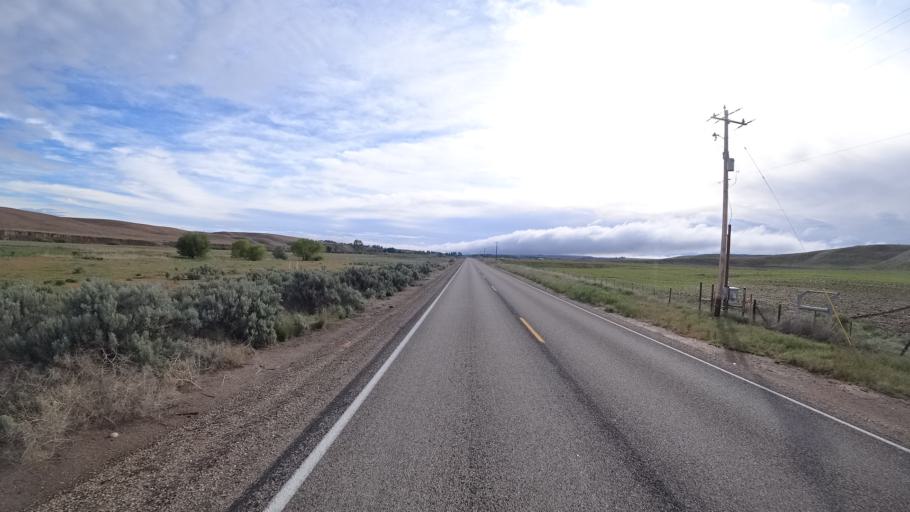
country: US
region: Idaho
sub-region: Ada County
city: Star
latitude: 43.7642
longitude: -116.5030
